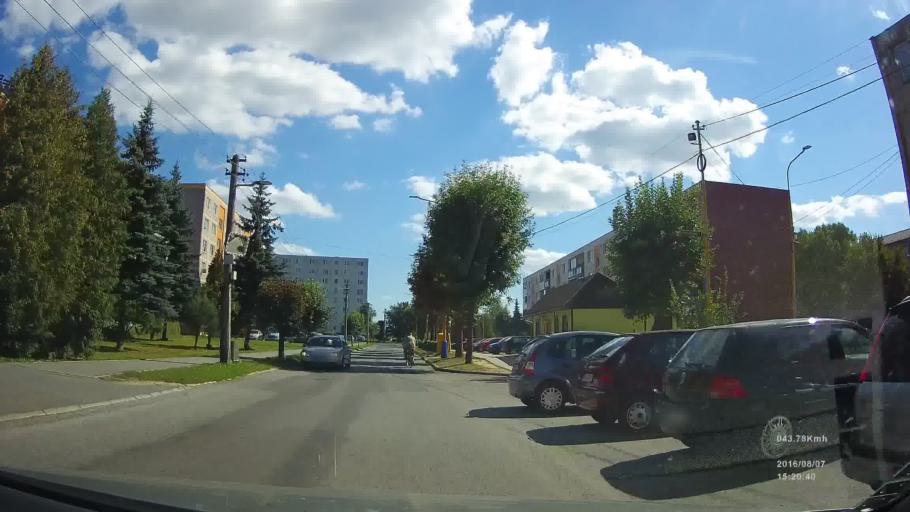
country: SK
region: Presovsky
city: Stropkov
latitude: 49.2005
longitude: 21.6484
